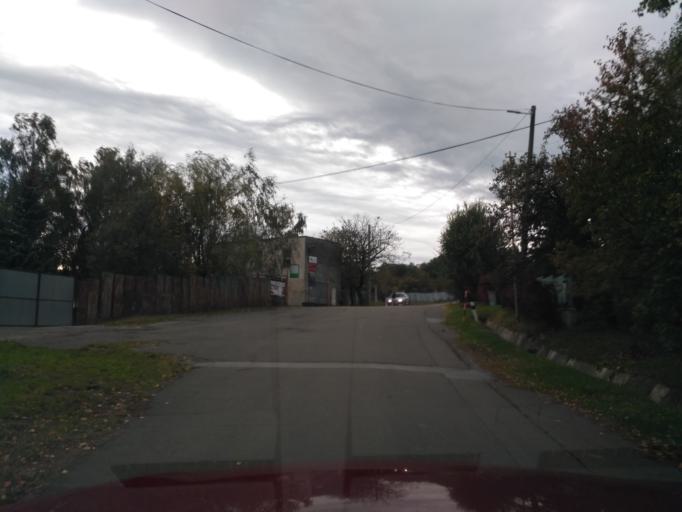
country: SK
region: Presovsky
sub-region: Okres Presov
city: Presov
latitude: 48.8885
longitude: 21.3231
